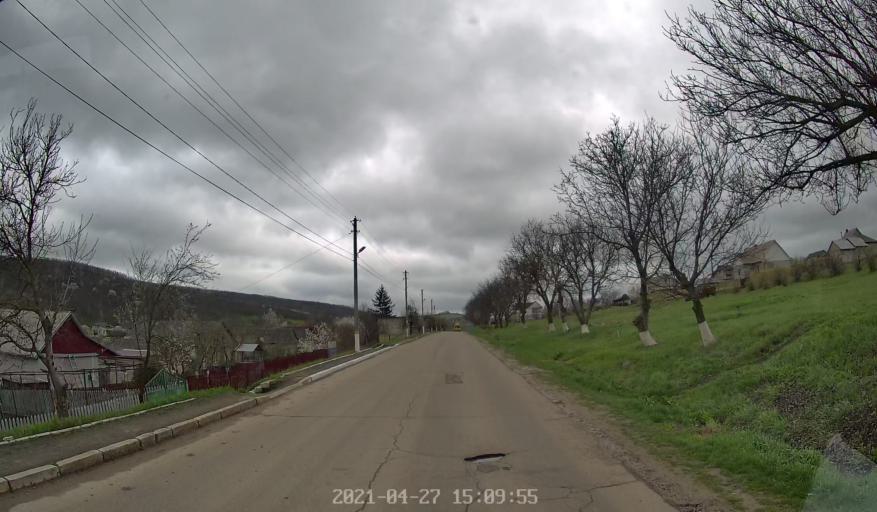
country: MD
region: Chisinau
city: Vadul lui Voda
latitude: 47.0454
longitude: 29.0335
